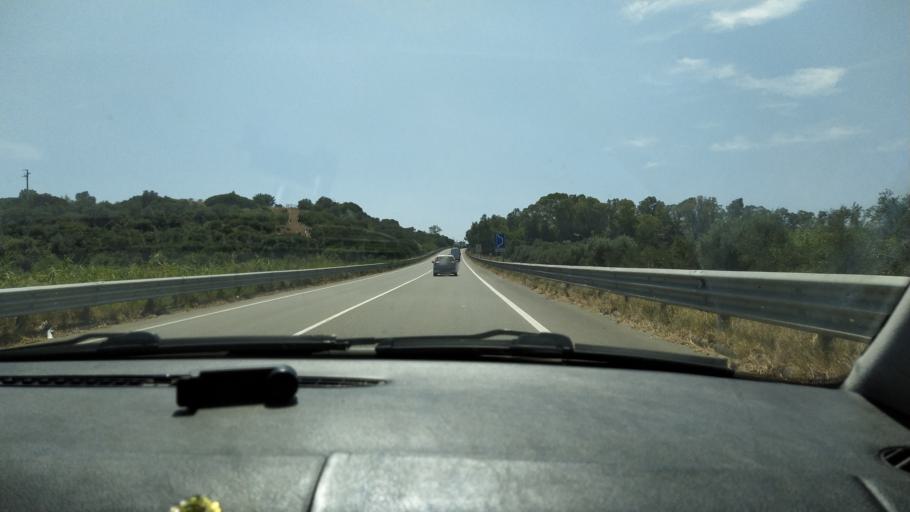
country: IT
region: Apulia
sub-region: Provincia di Taranto
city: Marina di Ginosa
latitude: 40.4298
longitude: 16.7942
